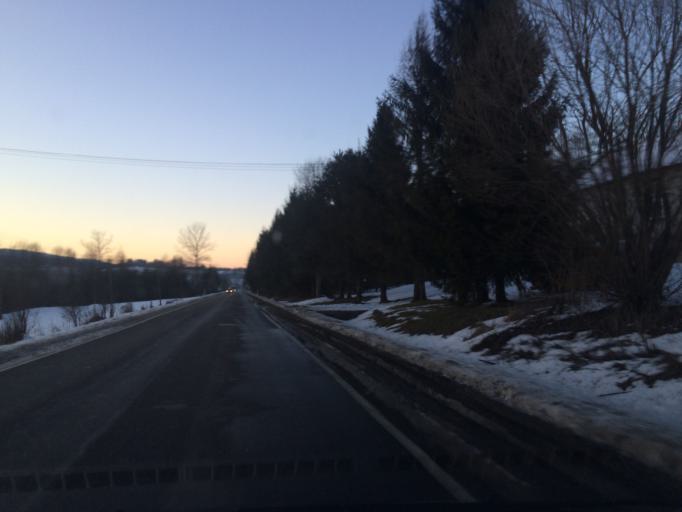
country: PL
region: Subcarpathian Voivodeship
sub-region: Powiat bieszczadzki
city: Czarna
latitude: 49.3703
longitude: 22.6528
